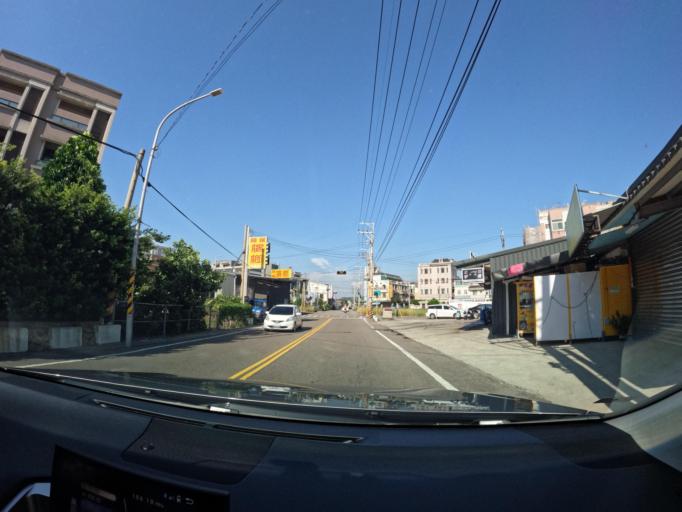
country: TW
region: Taiwan
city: Fengyuan
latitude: 24.2646
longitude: 120.5498
